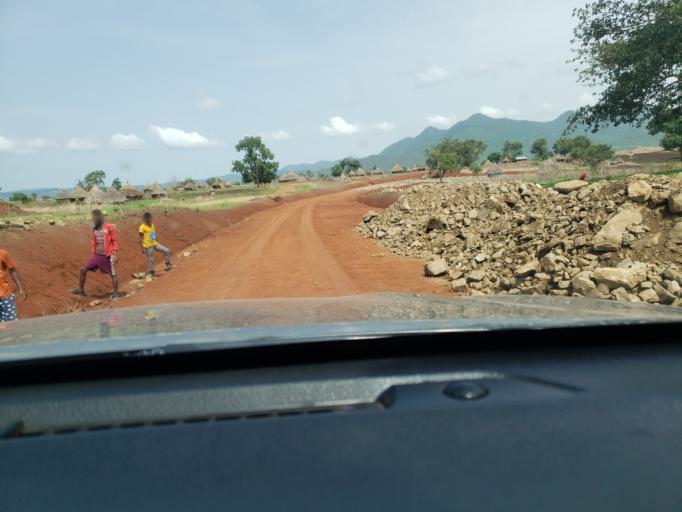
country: ET
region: Oromiya
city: Mendi
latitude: 10.1177
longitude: 35.1433
